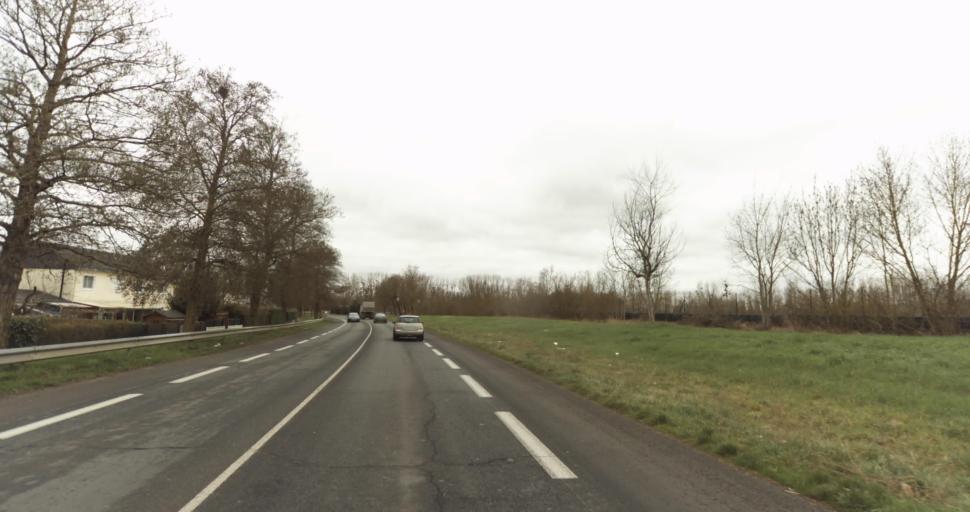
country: FR
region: Pays de la Loire
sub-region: Departement de Maine-et-Loire
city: Varrains
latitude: 47.2402
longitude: -0.0795
